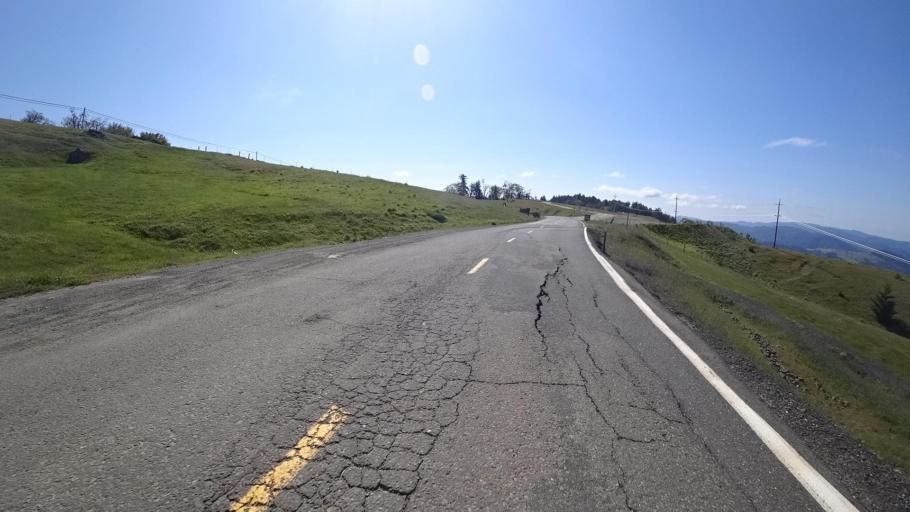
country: US
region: California
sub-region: Humboldt County
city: Redway
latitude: 40.1014
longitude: -123.6875
